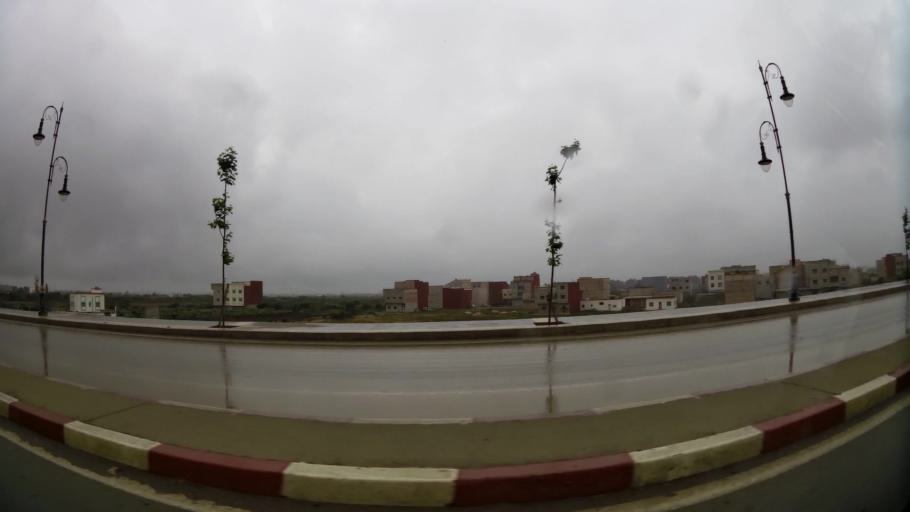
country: MA
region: Taza-Al Hoceima-Taounate
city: Imzourene
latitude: 35.1550
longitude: -3.8452
